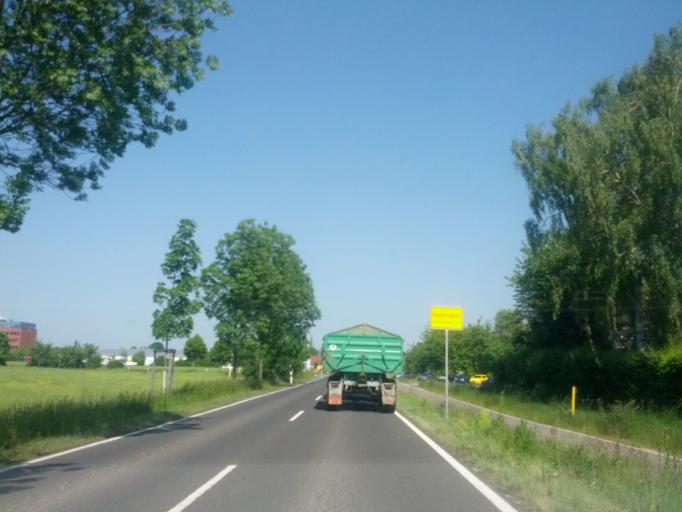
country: DE
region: Thuringia
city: Ingersleben
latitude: 50.9711
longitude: 10.9389
